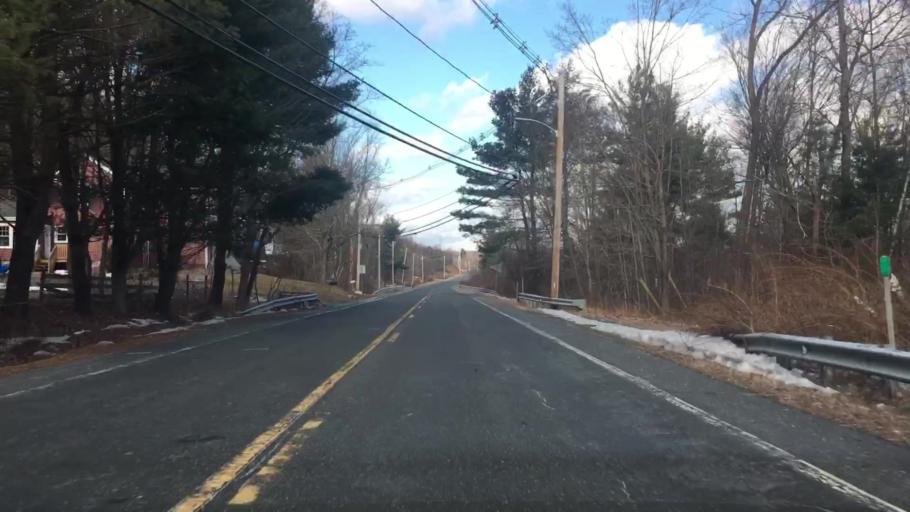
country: US
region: Massachusetts
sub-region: Hampden County
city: Brimfield
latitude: 42.1046
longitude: -72.2017
